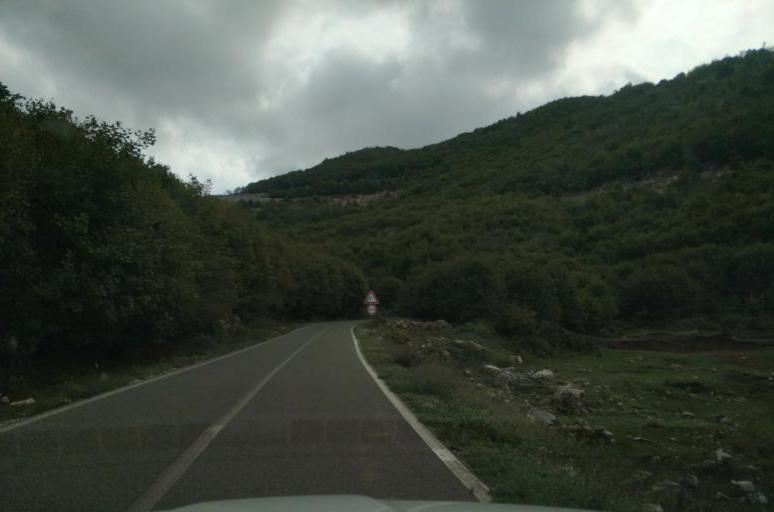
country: AL
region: Durres
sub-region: Rrethi i Krujes
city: Kruje
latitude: 41.5255
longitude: 19.8029
